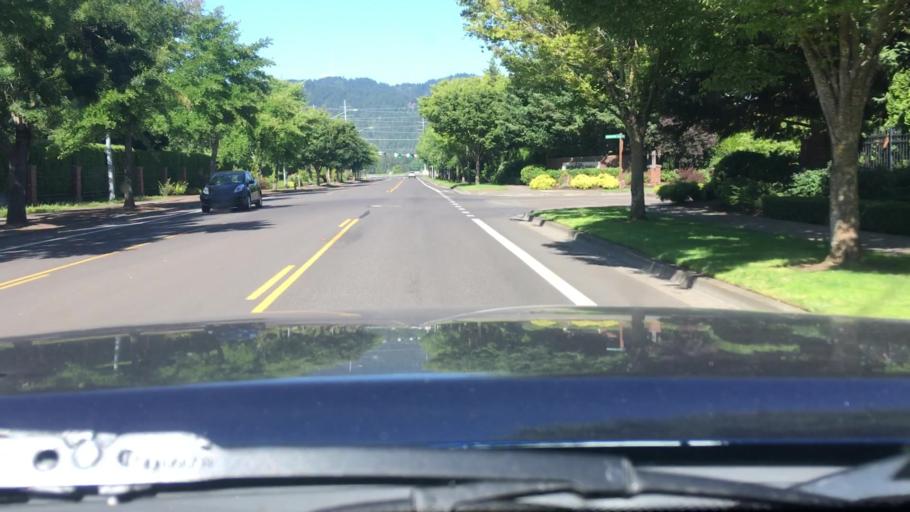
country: US
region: Oregon
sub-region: Lane County
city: Coburg
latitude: 44.0937
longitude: -123.0544
